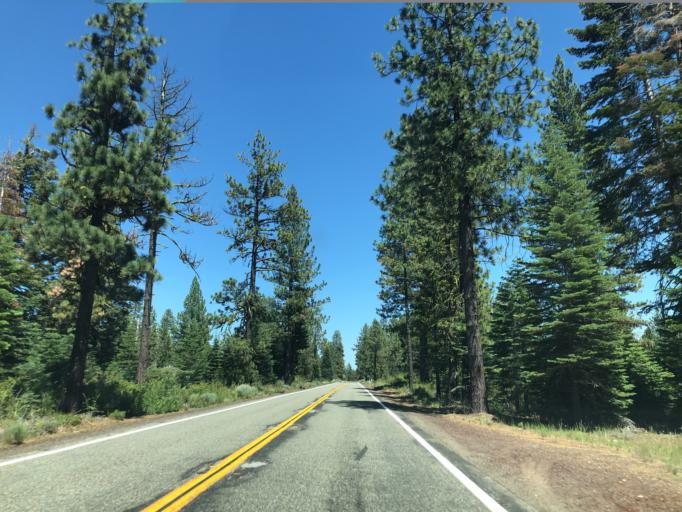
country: US
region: California
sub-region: Shasta County
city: Burney
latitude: 40.6155
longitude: -121.5026
